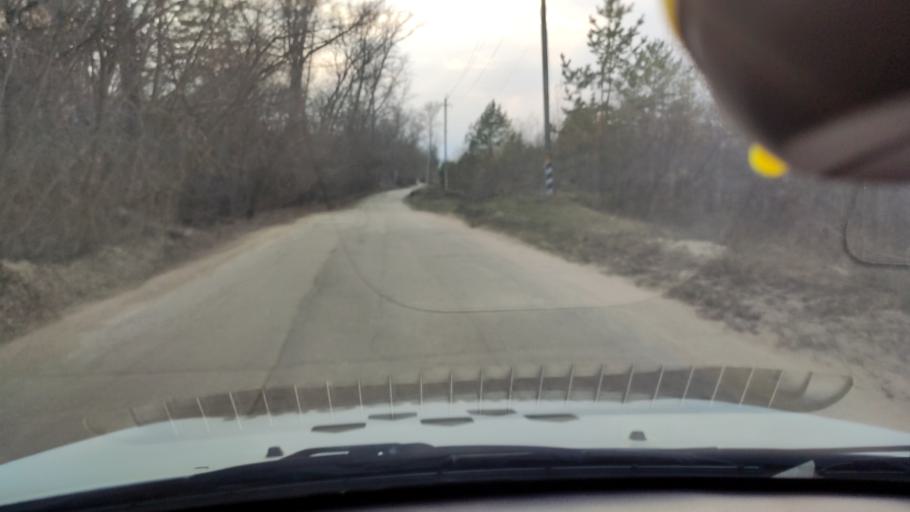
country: RU
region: Samara
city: Zhigulevsk
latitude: 53.4562
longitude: 49.5784
